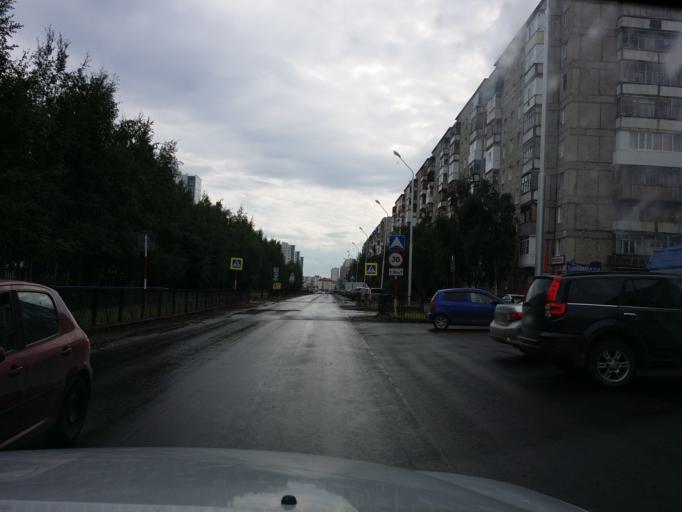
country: RU
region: Khanty-Mansiyskiy Avtonomnyy Okrug
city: Nizhnevartovsk
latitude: 60.9452
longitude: 76.5952
